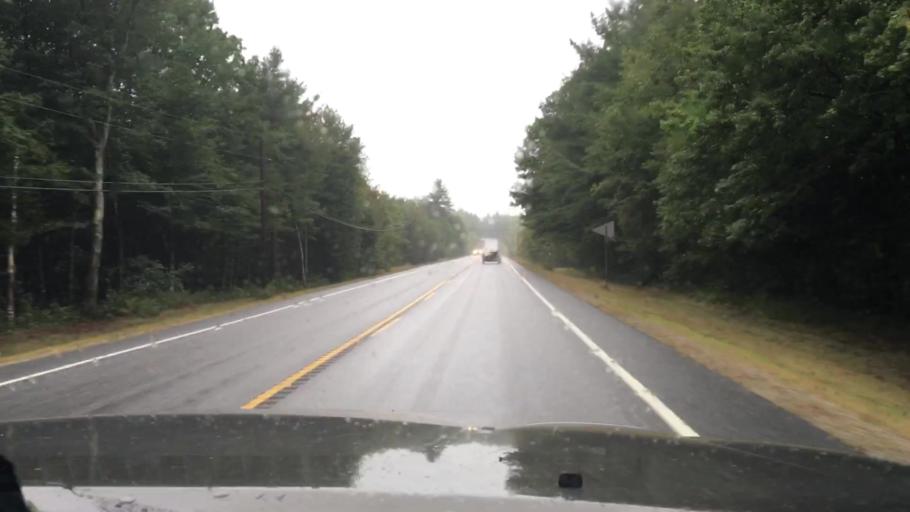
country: US
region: New Hampshire
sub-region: Cheshire County
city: Harrisville
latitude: 43.0371
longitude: -72.0928
